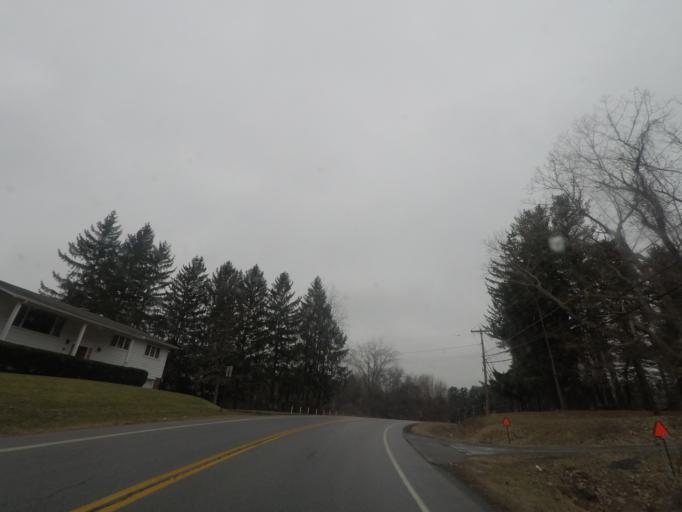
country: US
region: New York
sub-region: Saratoga County
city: Mechanicville
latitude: 42.8996
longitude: -73.7032
